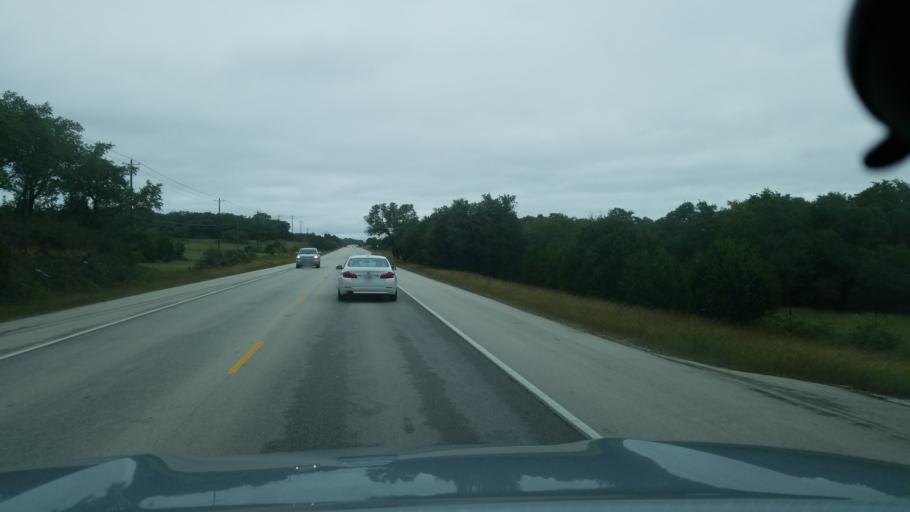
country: US
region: Texas
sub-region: Blanco County
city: Blanco
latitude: 30.0200
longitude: -98.4073
